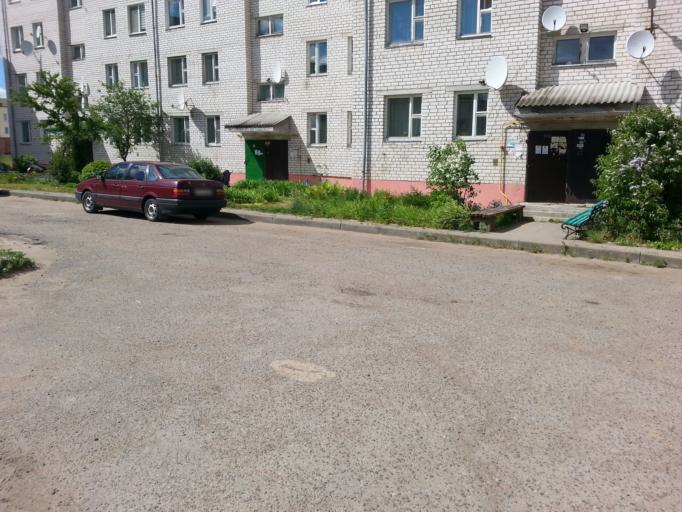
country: BY
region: Minsk
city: Narach
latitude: 54.9177
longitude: 26.6984
